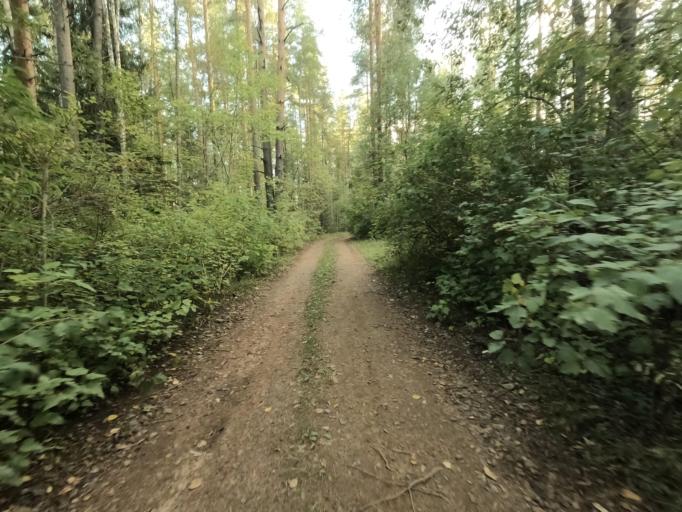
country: RU
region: Leningrad
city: Otradnoye
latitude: 59.8413
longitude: 30.7778
